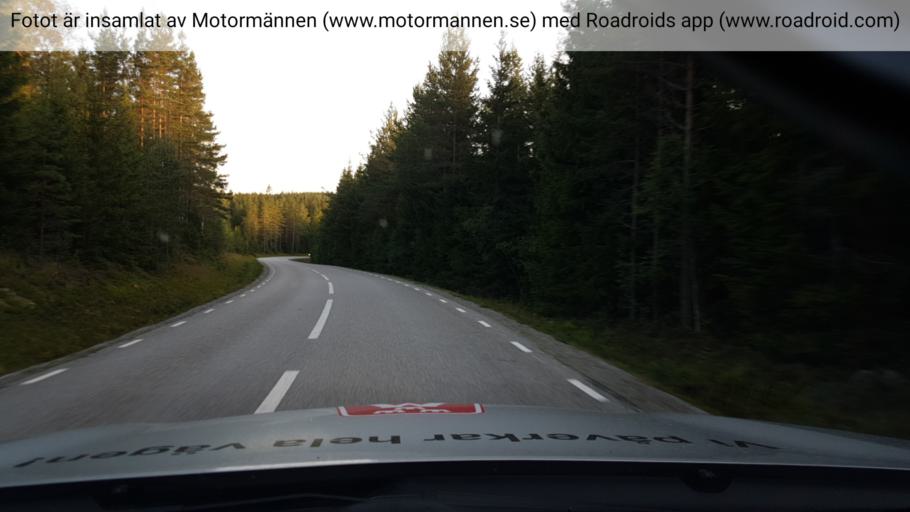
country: SE
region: OErebro
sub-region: Lindesbergs Kommun
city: Stora
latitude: 59.8970
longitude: 15.1878
